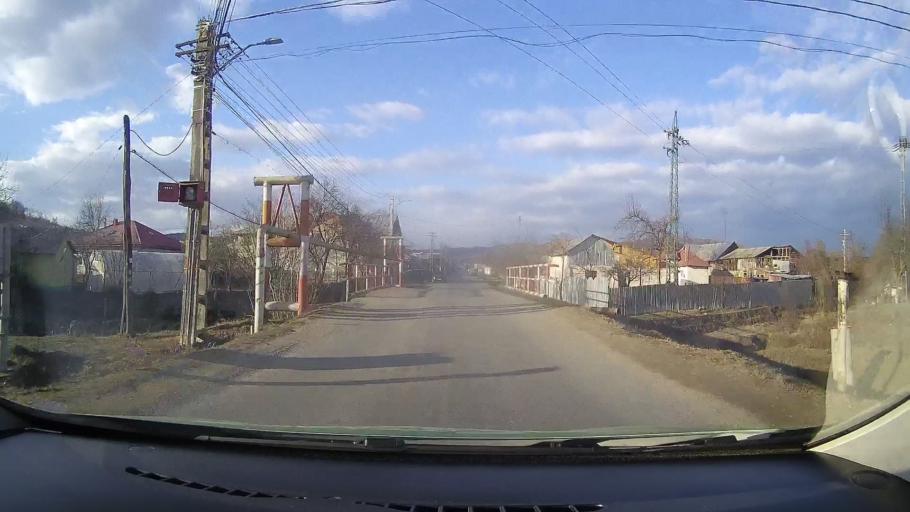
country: RO
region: Dambovita
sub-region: Comuna Ocnita
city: Ocnita
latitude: 44.9759
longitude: 25.5561
